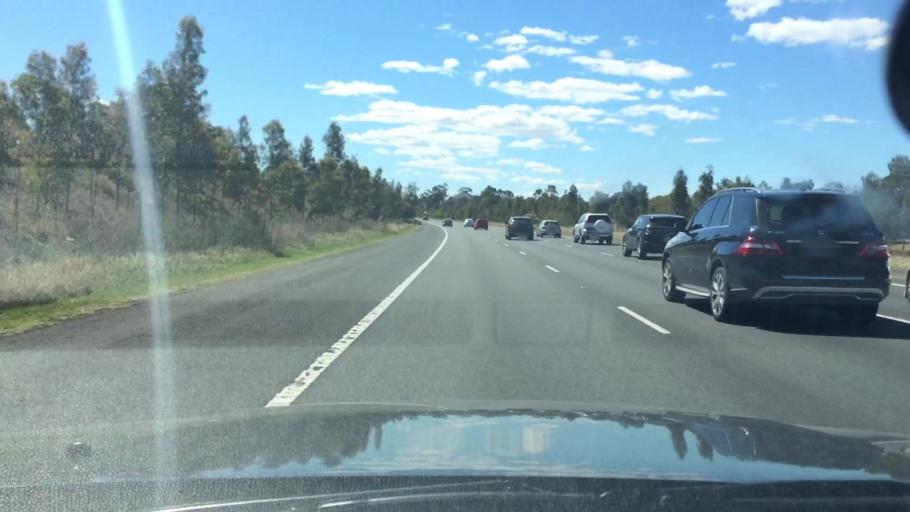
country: AU
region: New South Wales
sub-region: Campbelltown Municipality
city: Leumeah
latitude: -34.0425
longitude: 150.8210
